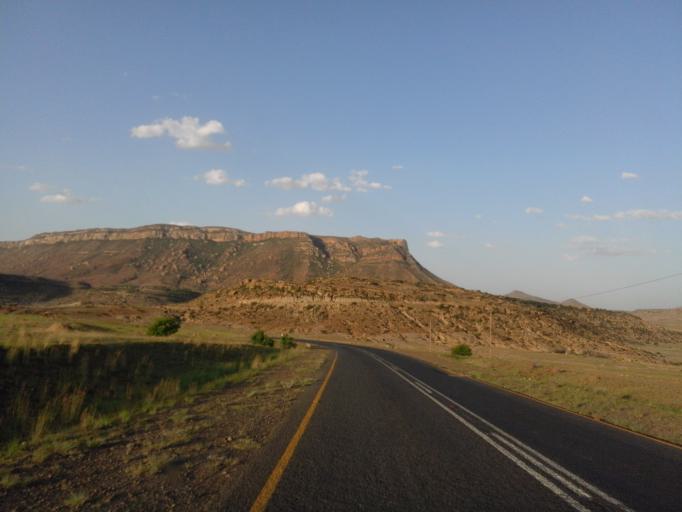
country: LS
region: Mafeteng
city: Mafeteng
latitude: -29.8967
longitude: 27.2547
